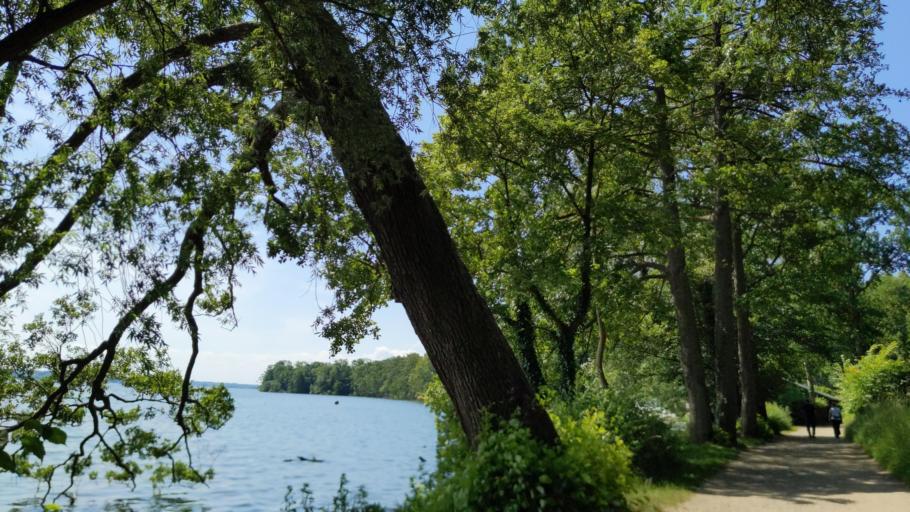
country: DE
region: Schleswig-Holstein
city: Ploen
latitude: 54.1528
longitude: 10.4096
